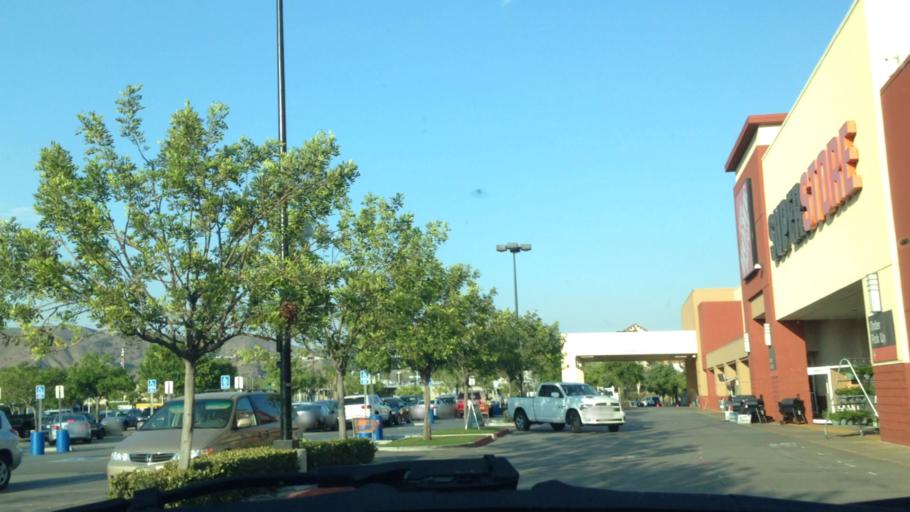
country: US
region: California
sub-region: Orange County
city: Yorba Linda
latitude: 33.8714
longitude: -117.7506
